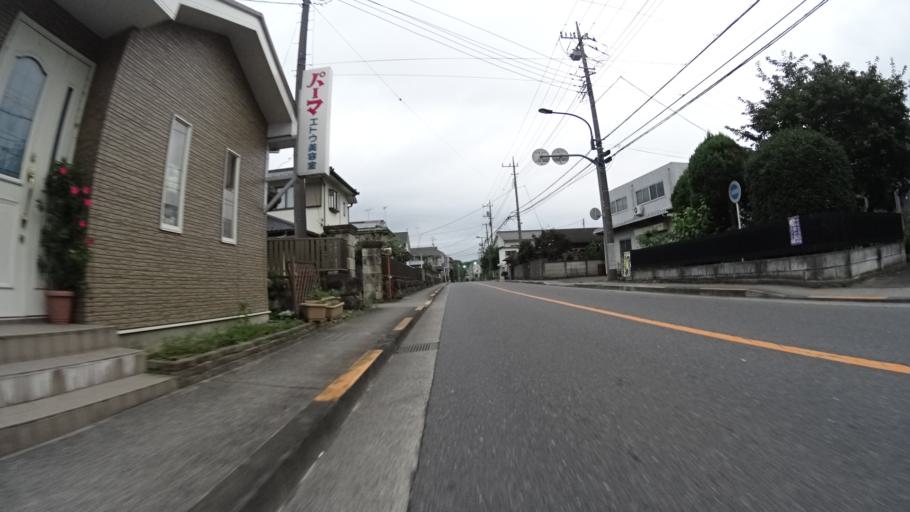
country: JP
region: Tokyo
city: Fussa
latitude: 35.7503
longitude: 139.3158
